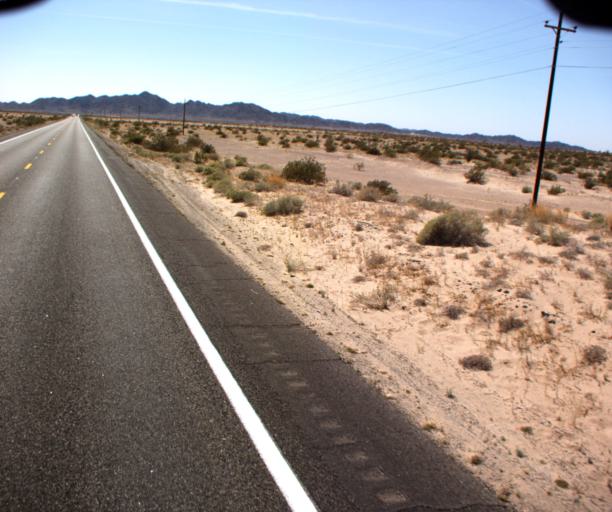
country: US
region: Arizona
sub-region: Yuma County
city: Fortuna Foothills
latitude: 32.8401
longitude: -114.3691
